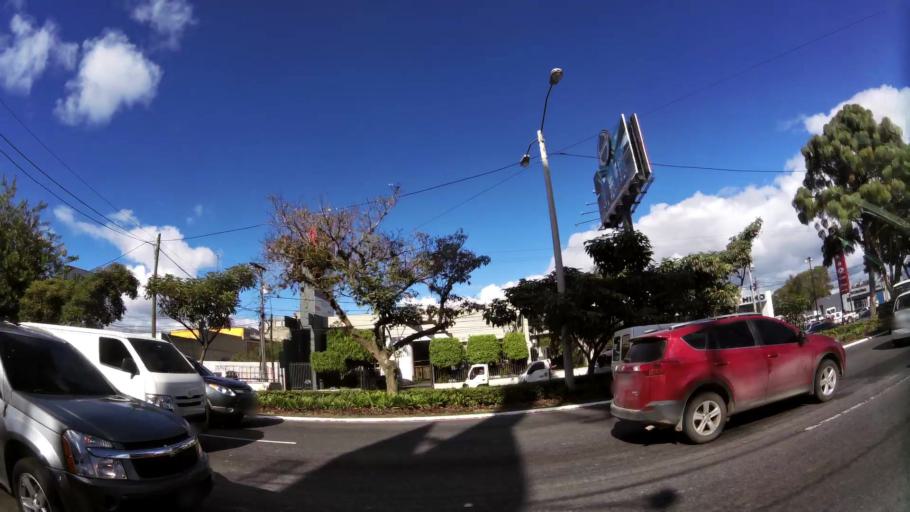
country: GT
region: Guatemala
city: Guatemala City
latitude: 14.6214
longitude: -90.5491
